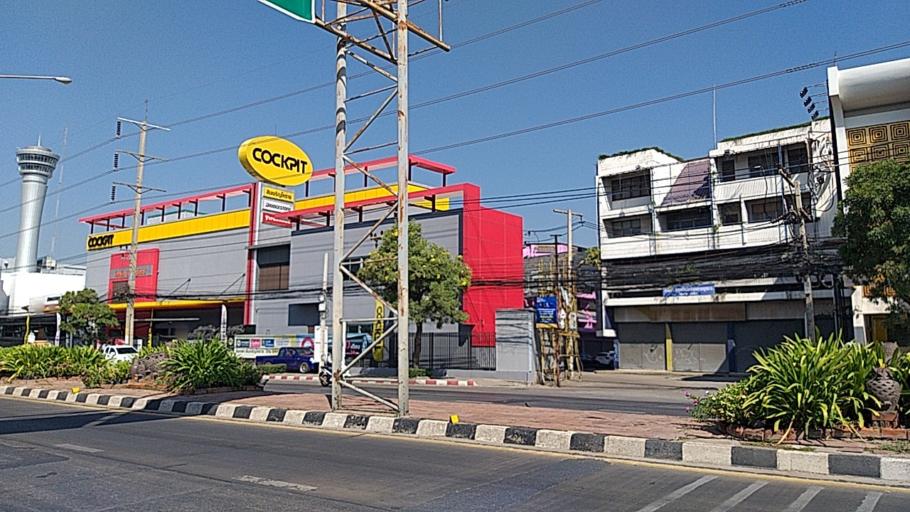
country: TH
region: Nakhon Ratchasima
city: Nakhon Ratchasima
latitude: 14.9798
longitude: 102.0937
